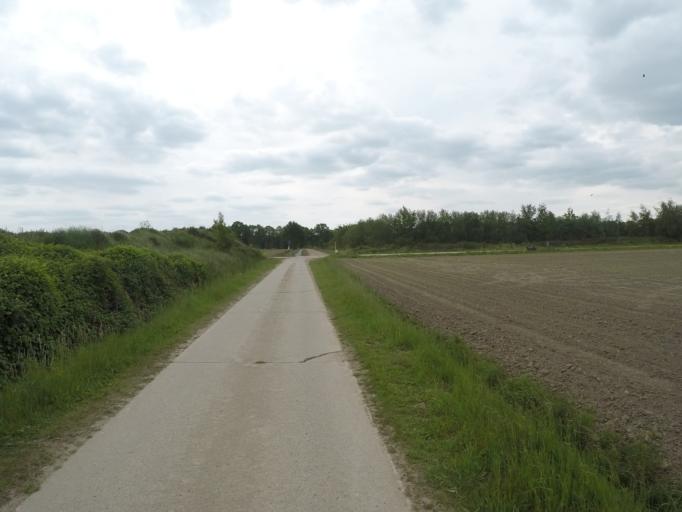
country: BE
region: Flanders
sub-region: Provincie Antwerpen
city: Oostmalle
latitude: 51.3241
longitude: 4.6946
